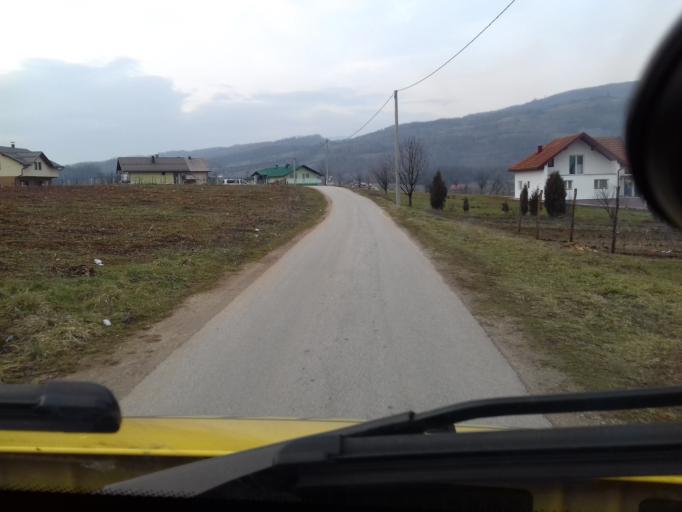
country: BA
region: Federation of Bosnia and Herzegovina
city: Gromiljak
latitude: 44.0182
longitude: 18.0174
